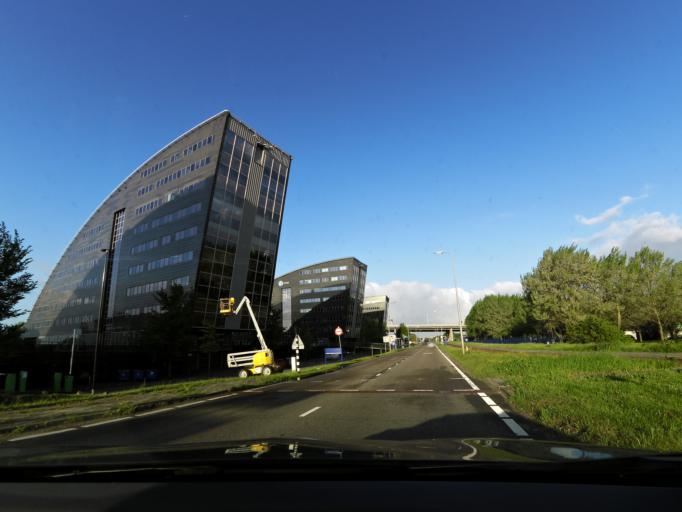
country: NL
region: South Holland
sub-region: Gemeente Rotterdam
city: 's-Gravenland
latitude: 51.9078
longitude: 4.5458
